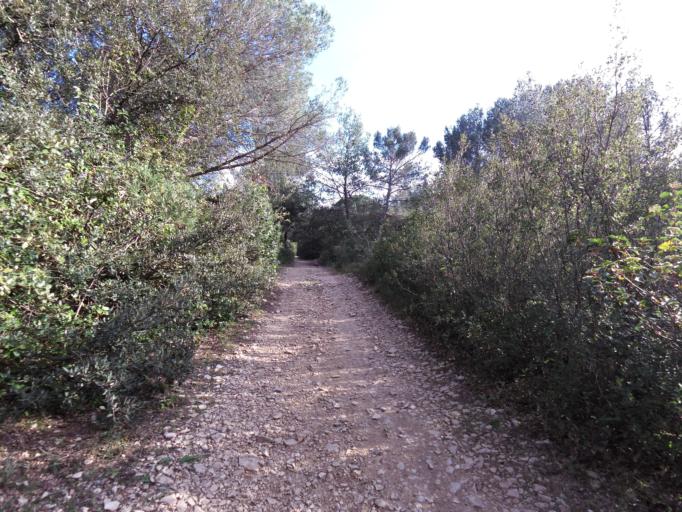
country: FR
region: Languedoc-Roussillon
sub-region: Departement du Gard
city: Congenies
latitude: 43.7843
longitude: 4.1747
